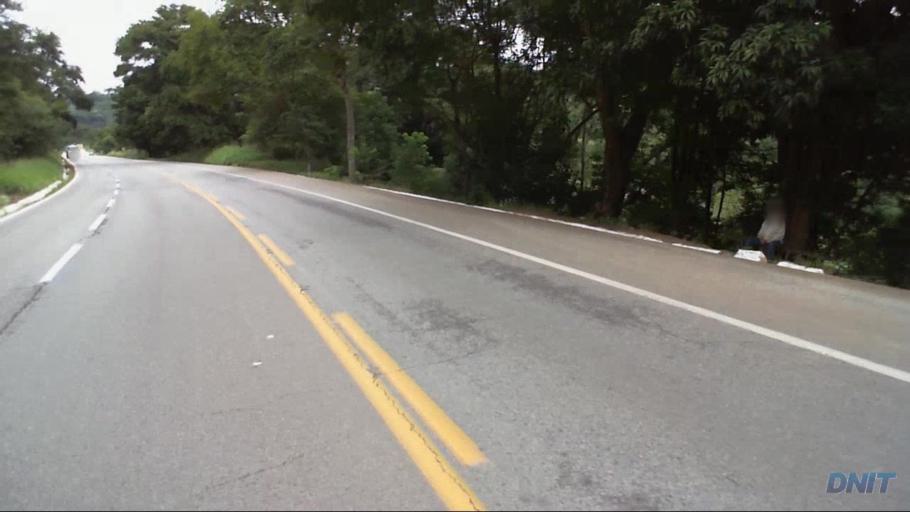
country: BR
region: Minas Gerais
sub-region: Barao De Cocais
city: Barao de Cocais
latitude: -19.7997
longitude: -43.4148
